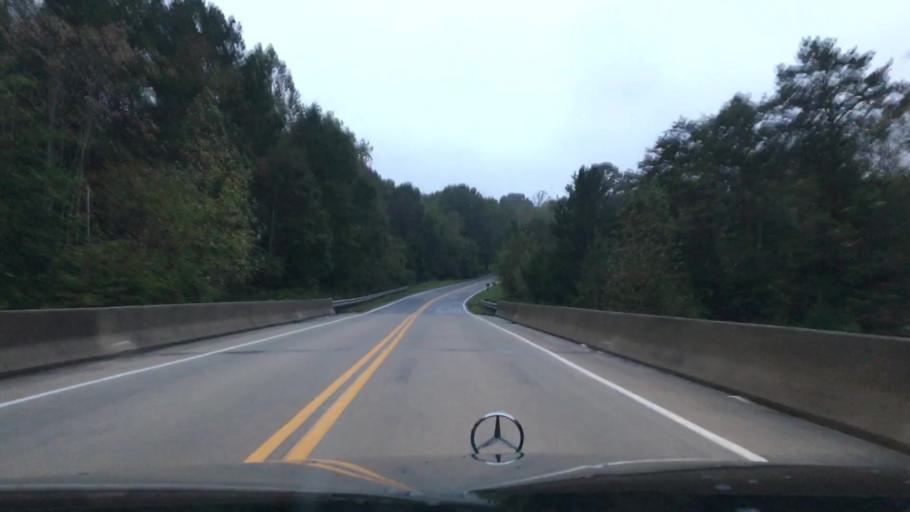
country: US
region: Virginia
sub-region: Campbell County
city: Timberlake
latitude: 37.2417
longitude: -79.2804
